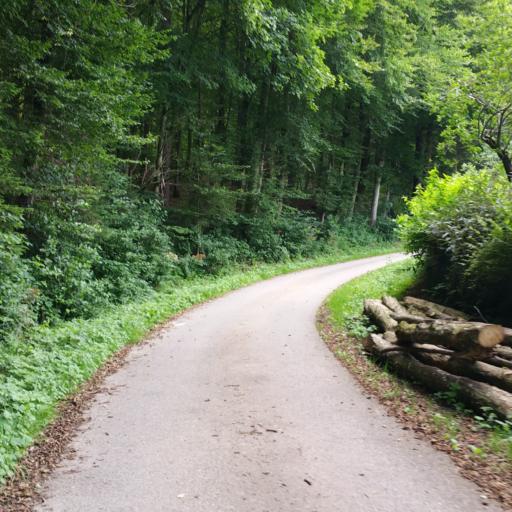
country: AT
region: Styria
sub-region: Politischer Bezirk Leibnitz
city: Gleinstatten
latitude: 46.7444
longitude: 15.3731
